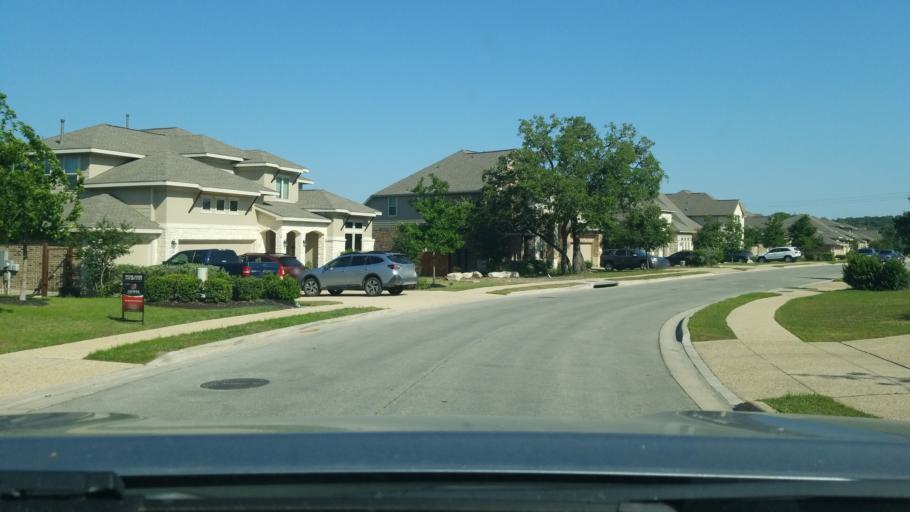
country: US
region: Texas
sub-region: Comal County
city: Bulverde
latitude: 29.7738
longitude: -98.4204
